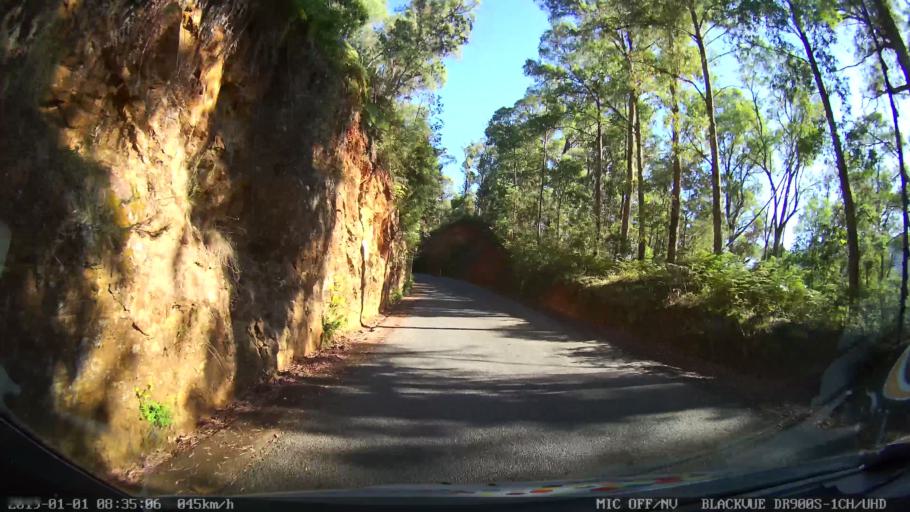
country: AU
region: New South Wales
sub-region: Snowy River
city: Jindabyne
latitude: -36.3510
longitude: 148.1932
